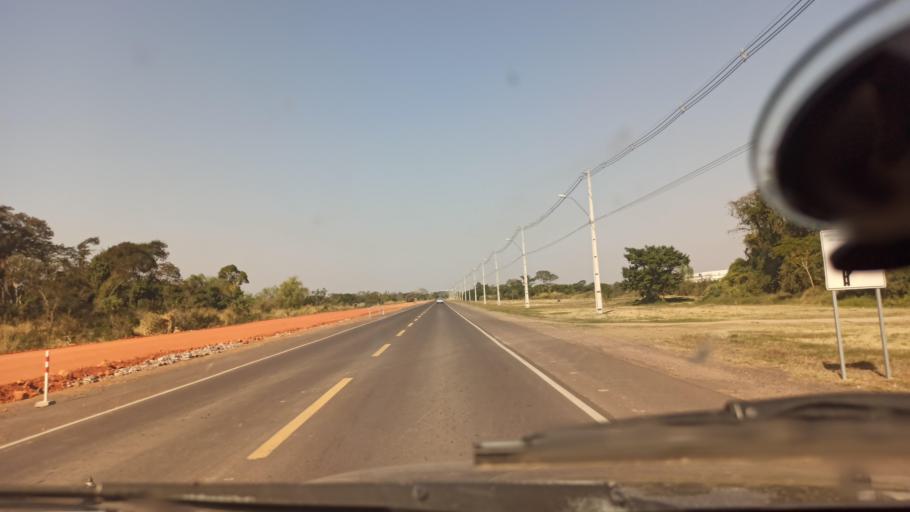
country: PY
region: Central
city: Colonia Mariano Roque Alonso
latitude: -25.1903
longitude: -57.5798
